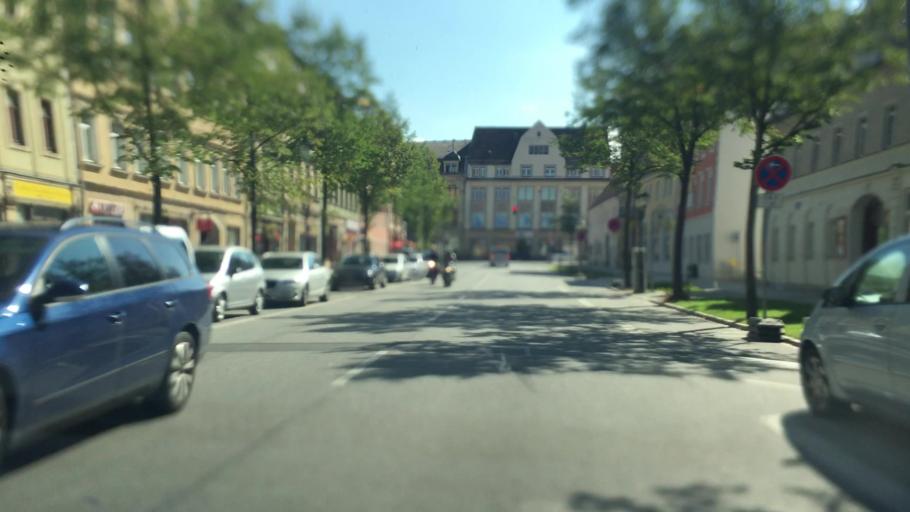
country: DE
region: Saxony
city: Pirna
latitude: 50.9590
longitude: 13.9390
